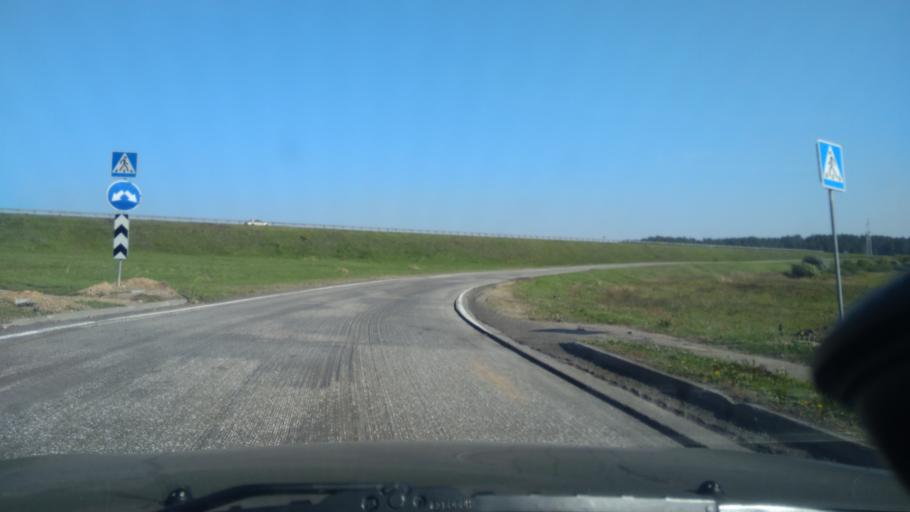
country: BY
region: Minsk
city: Rakaw
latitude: 53.9769
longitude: 27.0420
